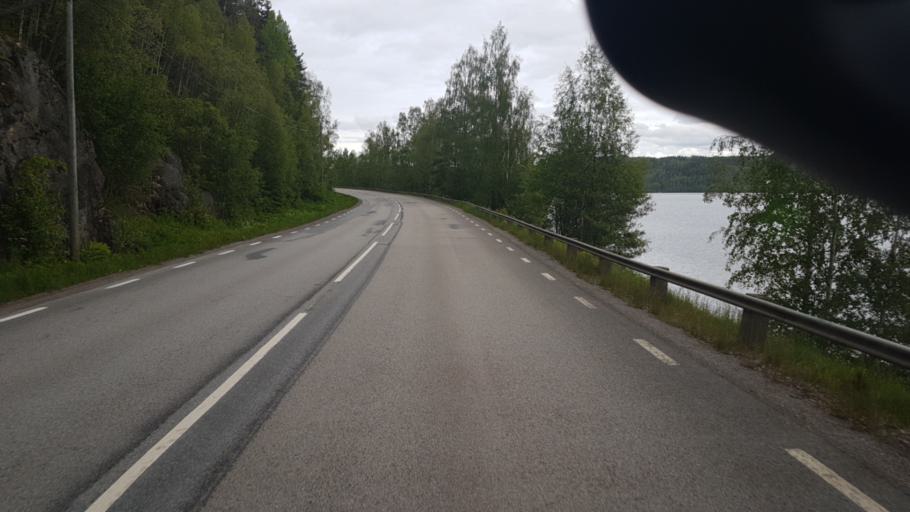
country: SE
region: Vaermland
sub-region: Arvika Kommun
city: Arvika
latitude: 59.7078
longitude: 12.6358
